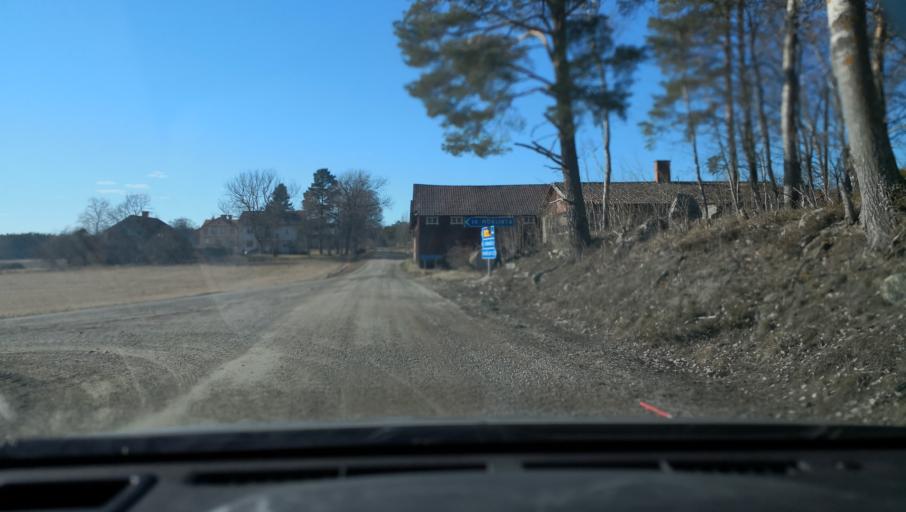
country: SE
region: Vaestmanland
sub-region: Sala Kommun
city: Sala
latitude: 60.1518
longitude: 16.6369
